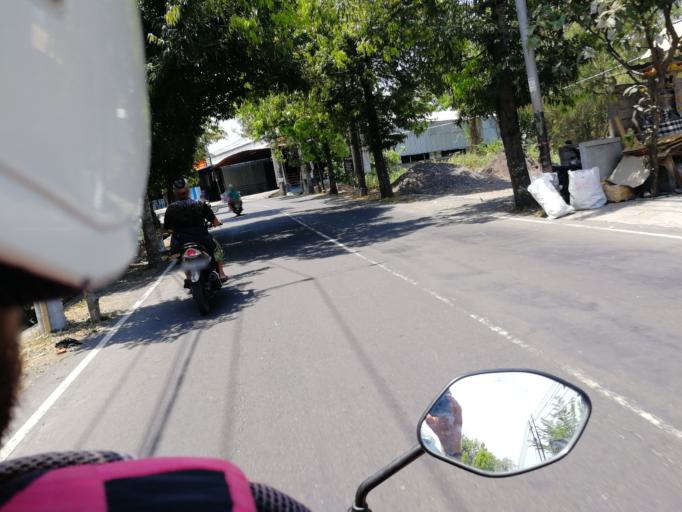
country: ID
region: Bali
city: Subagan
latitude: -8.4531
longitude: 115.5962
